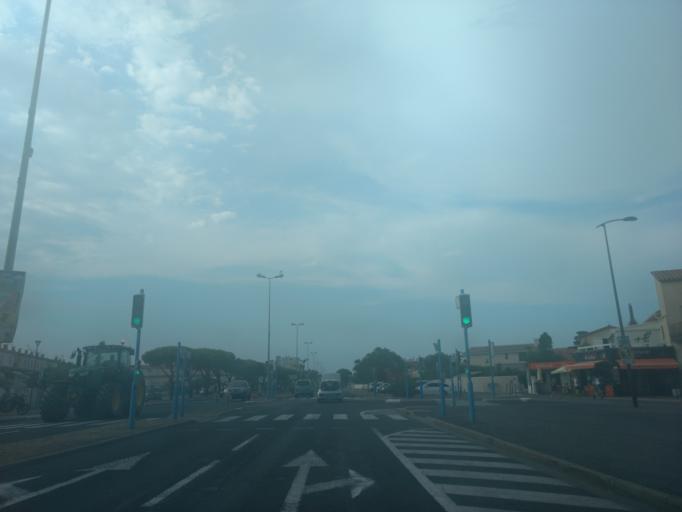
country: FR
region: Languedoc-Roussillon
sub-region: Departement des Pyrenees-Orientales
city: Saint-Cyprien-Plage
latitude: 42.6330
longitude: 3.0328
